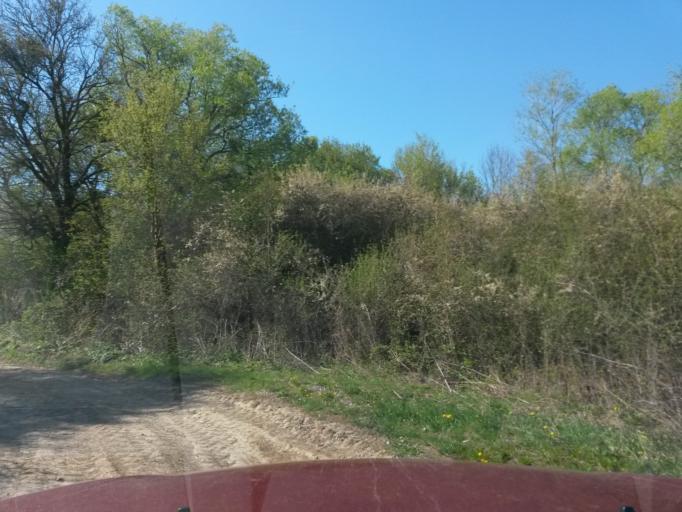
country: SK
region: Kosicky
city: Secovce
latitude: 48.6177
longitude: 21.5429
